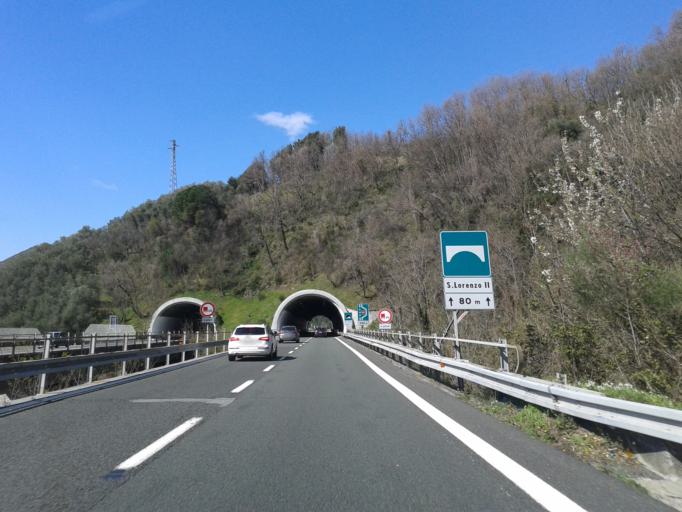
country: IT
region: Liguria
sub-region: Provincia di Genova
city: Moneglia
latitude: 44.2549
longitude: 9.4958
